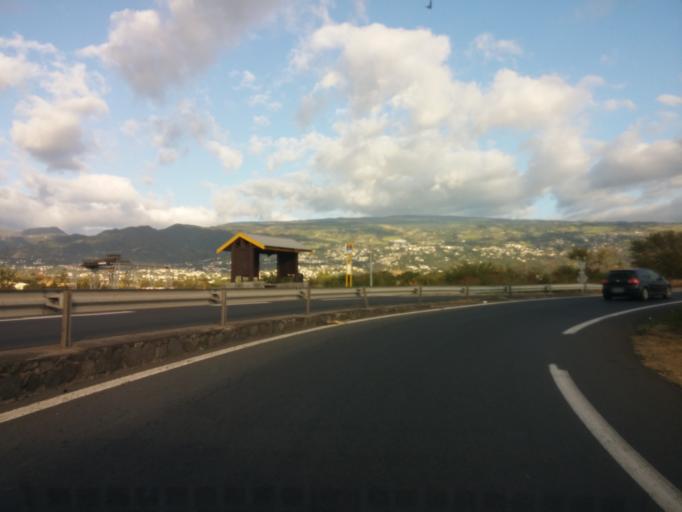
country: RE
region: Reunion
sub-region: Reunion
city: Le Port
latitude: -20.9706
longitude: 55.2990
